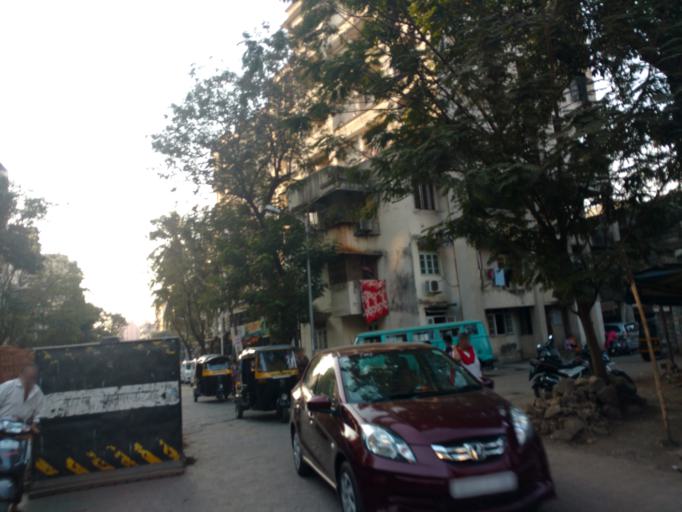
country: IN
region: Maharashtra
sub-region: Mumbai Suburban
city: Borivli
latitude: 19.2034
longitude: 72.8426
